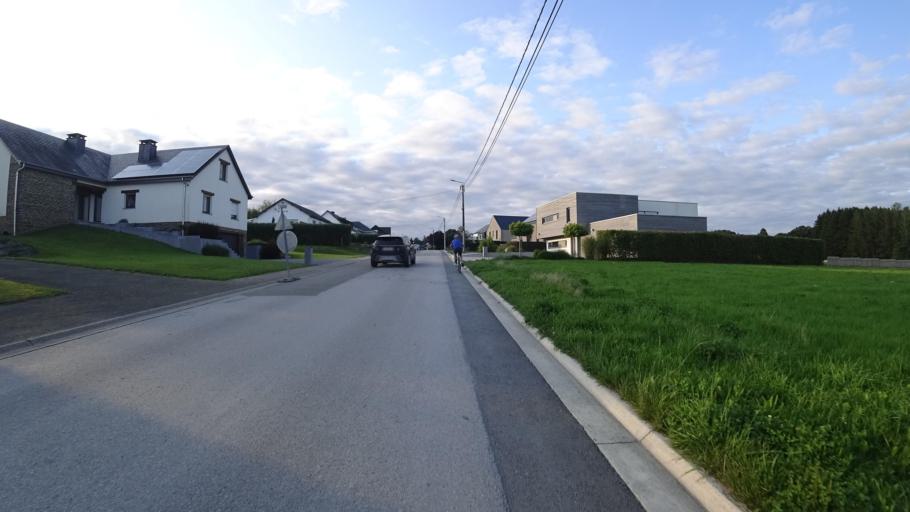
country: BE
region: Wallonia
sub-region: Province du Luxembourg
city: Neufchateau
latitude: 49.9067
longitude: 5.3871
